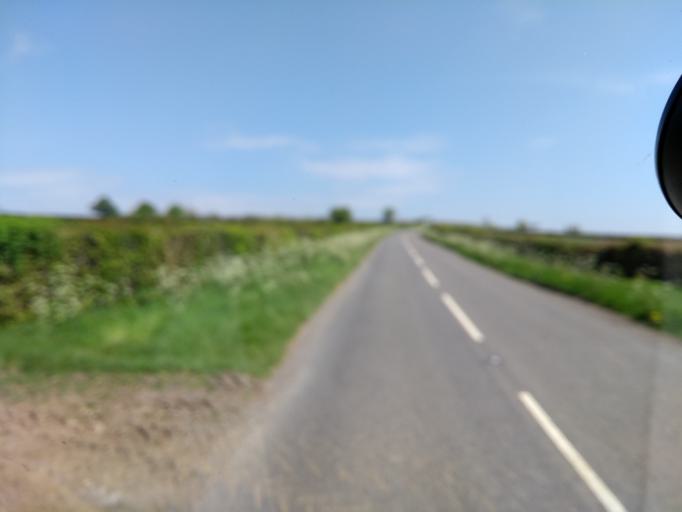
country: GB
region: England
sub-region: Somerset
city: Chard
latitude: 50.9017
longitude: -3.0074
